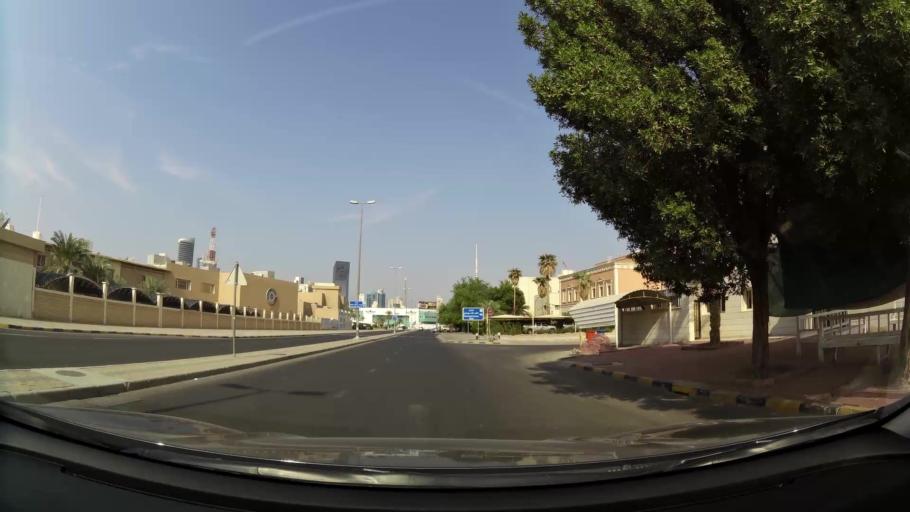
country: KW
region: Al Asimah
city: Ash Shamiyah
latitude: 29.3527
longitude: 47.9652
